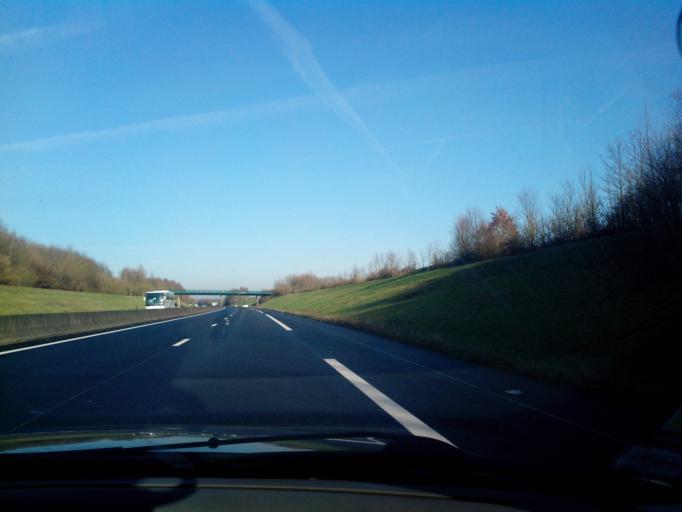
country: FR
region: Picardie
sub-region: Departement de l'Oise
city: Saint-Sulpice
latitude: 49.3387
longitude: 2.1046
